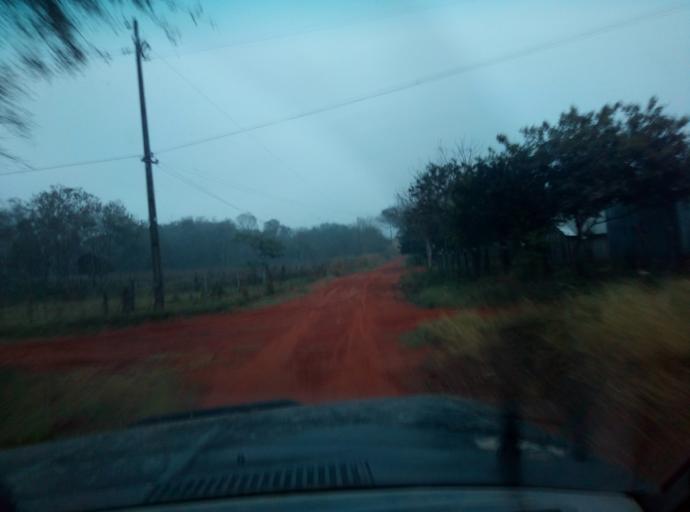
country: PY
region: Caaguazu
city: Doctor Cecilio Baez
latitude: -25.1594
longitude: -56.2616
